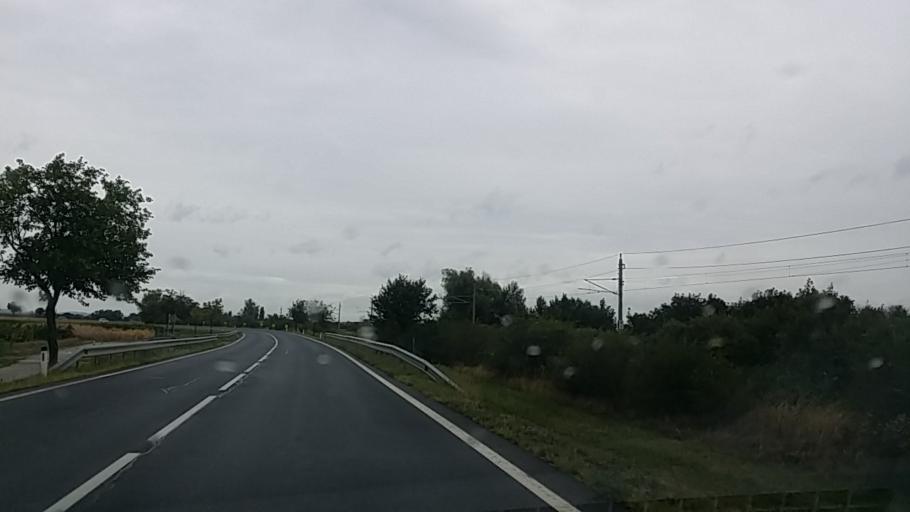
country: AT
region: Burgenland
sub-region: Eisenstadt-Umgebung
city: Schutzen am Gebirge
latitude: 47.8608
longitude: 16.6430
